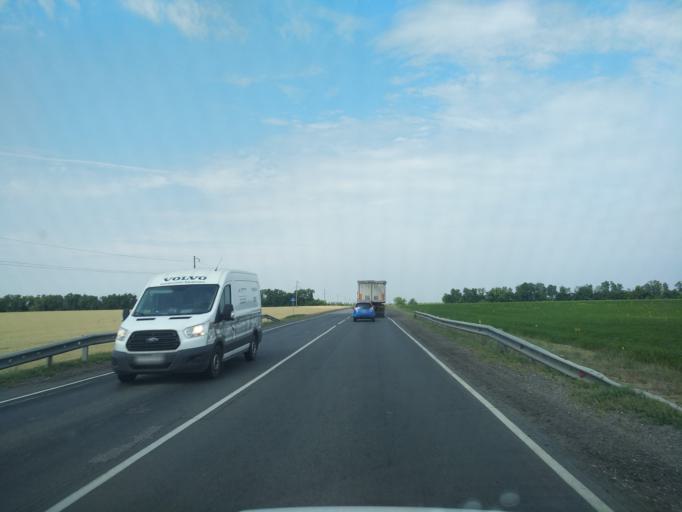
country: RU
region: Voronezj
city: Orlovo
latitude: 51.6831
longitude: 39.5607
